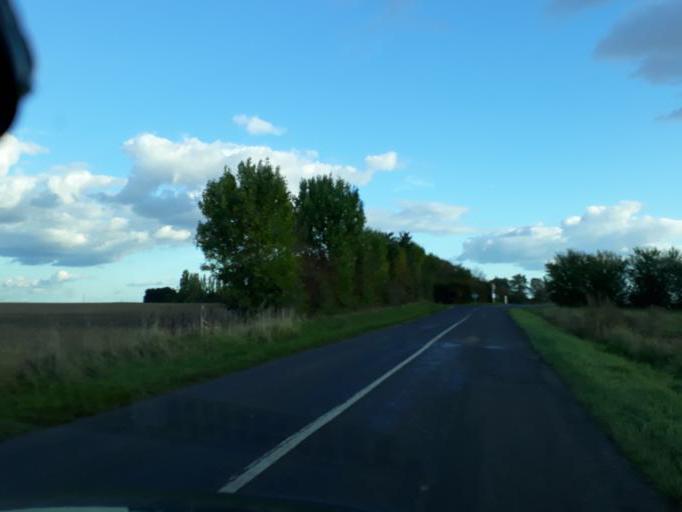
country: FR
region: Centre
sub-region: Departement du Loir-et-Cher
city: Mer
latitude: 47.8048
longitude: 1.5127
